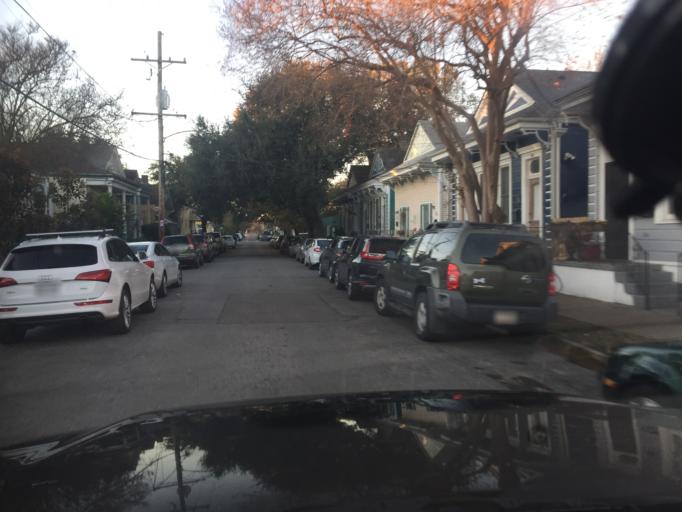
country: US
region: Louisiana
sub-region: Orleans Parish
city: New Orleans
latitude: 29.9772
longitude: -90.0873
